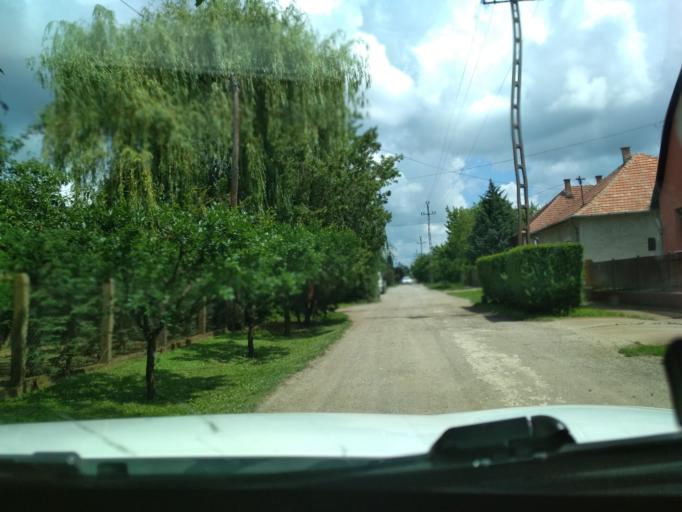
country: HU
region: Jasz-Nagykun-Szolnok
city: Tiszafured
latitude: 47.6125
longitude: 20.7445
